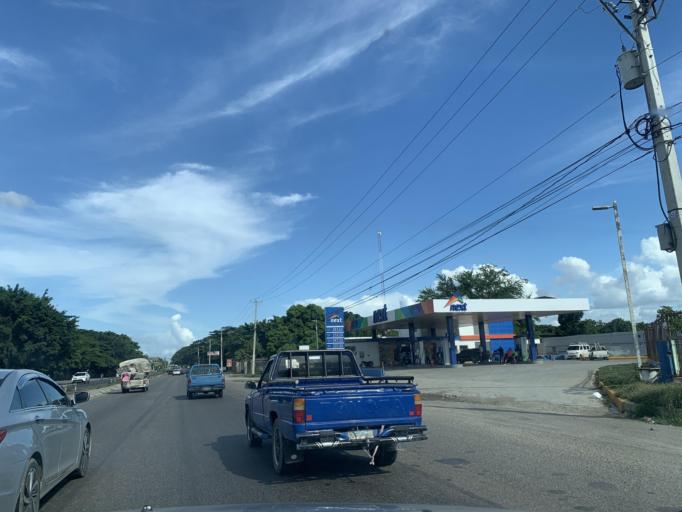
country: DO
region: Santiago
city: Villa Gonzalez
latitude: 19.5400
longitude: -70.7952
